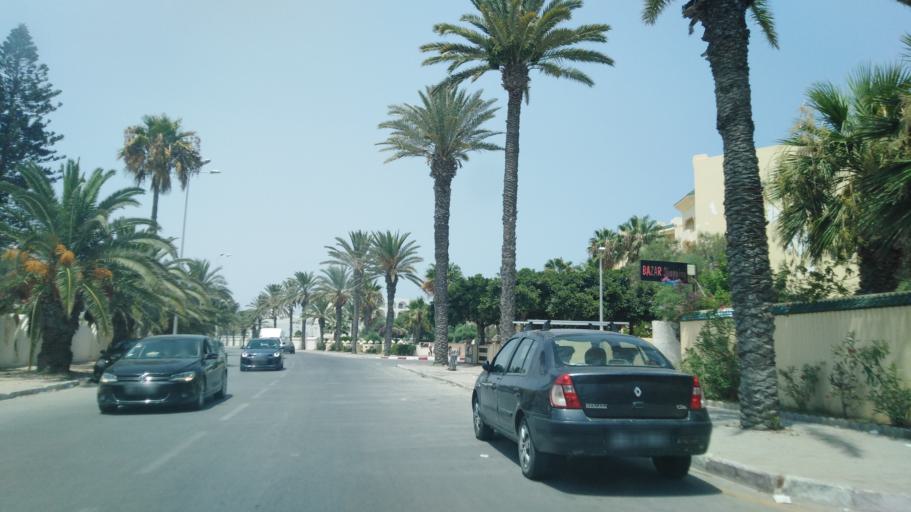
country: TN
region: Al Mahdiyah
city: Mahdia
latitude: 35.5148
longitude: 11.0468
